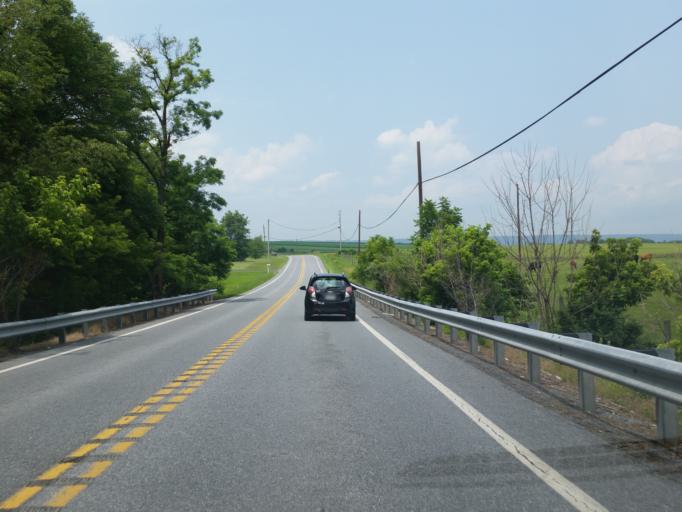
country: US
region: Pennsylvania
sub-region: Lebanon County
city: Palmyra
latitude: 40.3589
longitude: -76.6203
